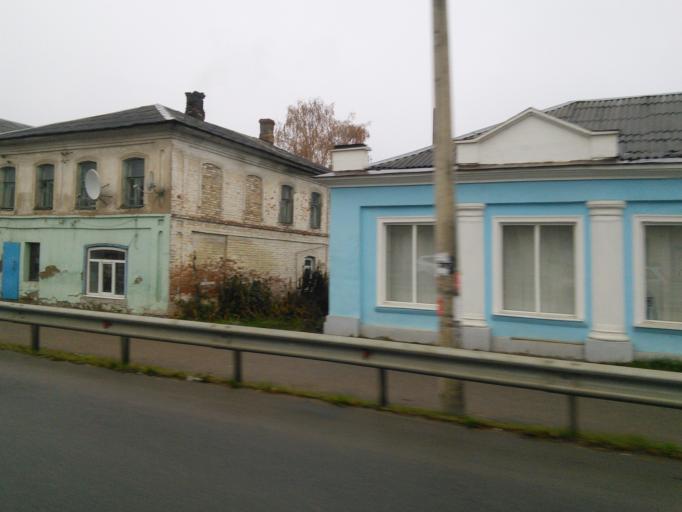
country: RU
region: Jaroslavl
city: Petrovsk
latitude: 57.0130
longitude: 39.2633
